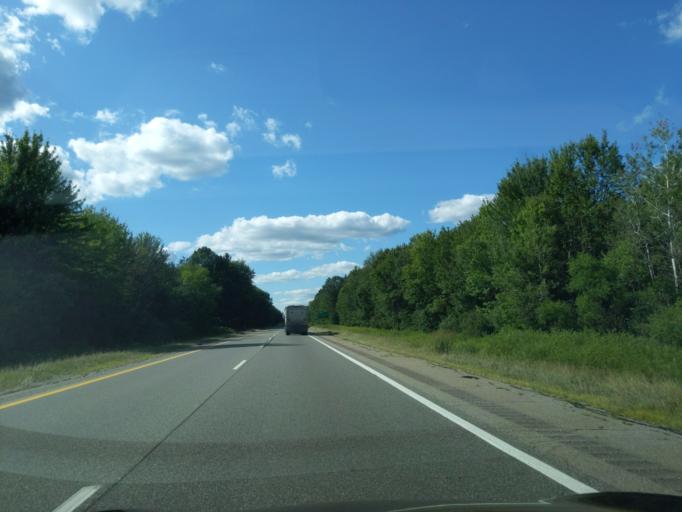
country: US
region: Michigan
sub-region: Muskegon County
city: Fruitport
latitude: 43.1057
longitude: -86.1152
